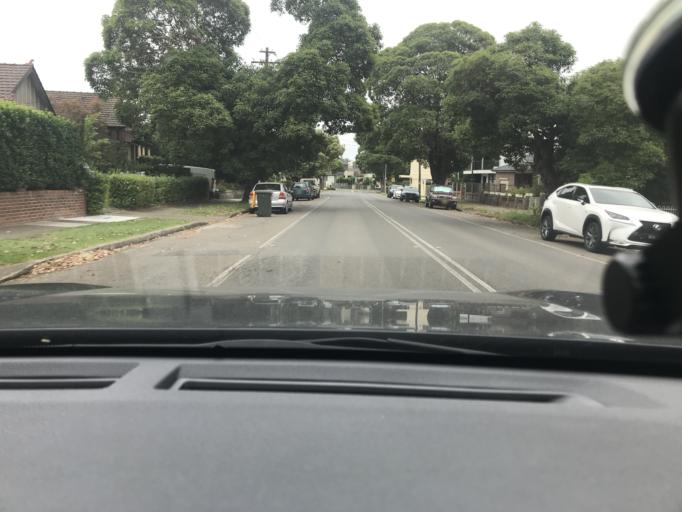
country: AU
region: New South Wales
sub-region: Canada Bay
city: Concord
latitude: -33.8606
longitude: 151.1102
